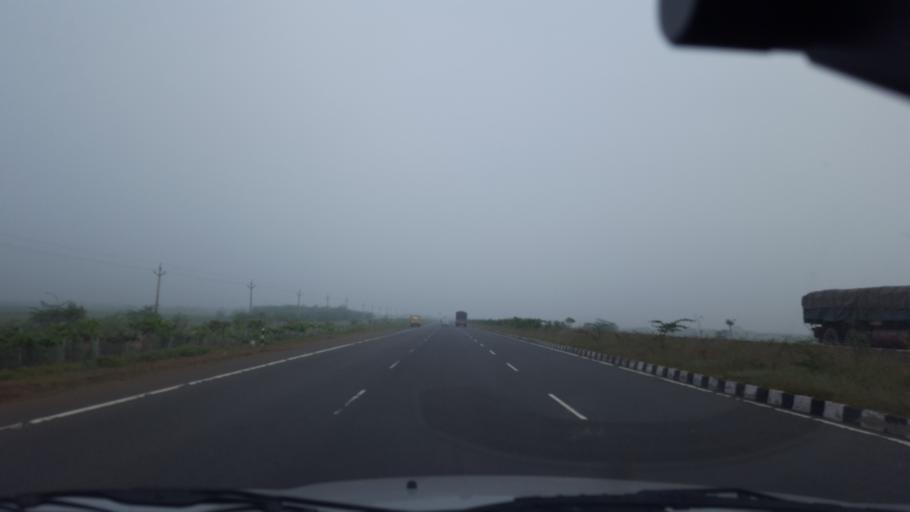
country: IN
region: Andhra Pradesh
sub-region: Prakasam
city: Ongole
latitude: 15.4851
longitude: 80.0629
